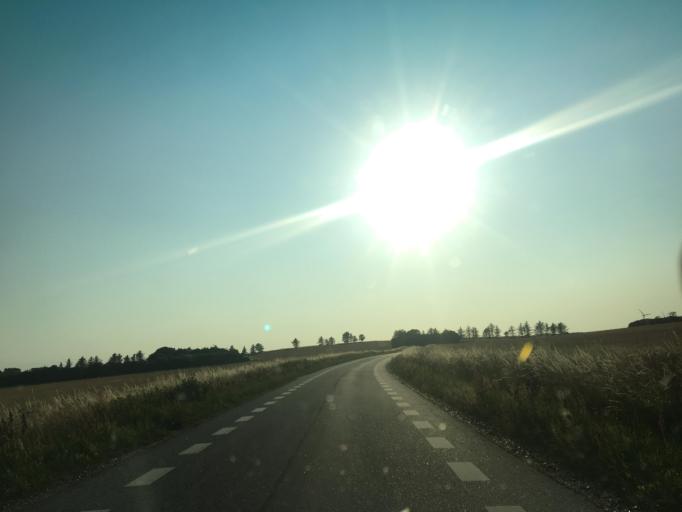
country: DK
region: North Denmark
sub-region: Thisted Kommune
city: Hurup
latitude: 56.8166
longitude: 8.3742
